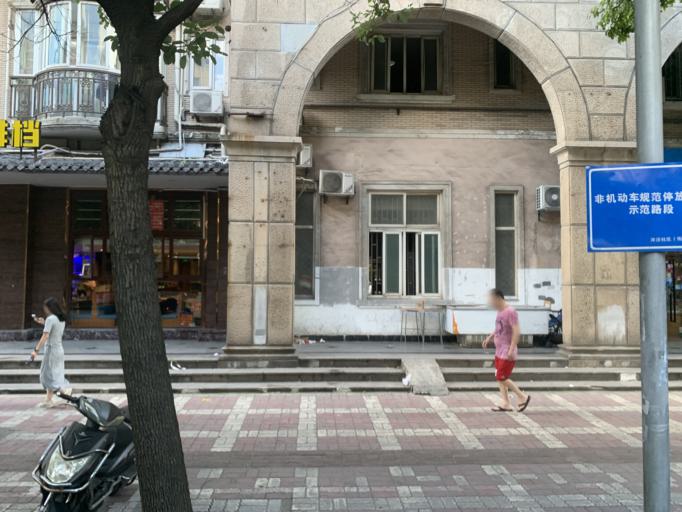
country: CN
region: Shanghai Shi
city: Pudong
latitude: 31.2469
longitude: 121.5506
